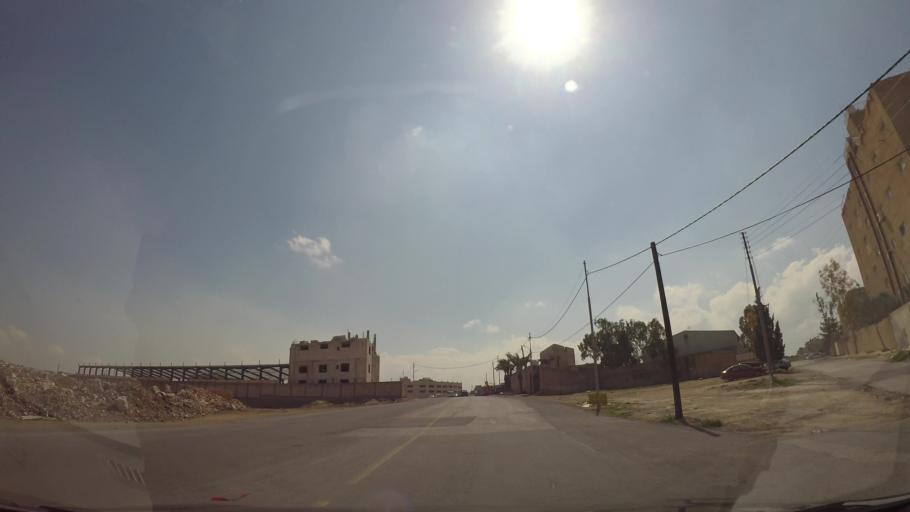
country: JO
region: Zarqa
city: Russeifa
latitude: 31.9864
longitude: 36.0094
